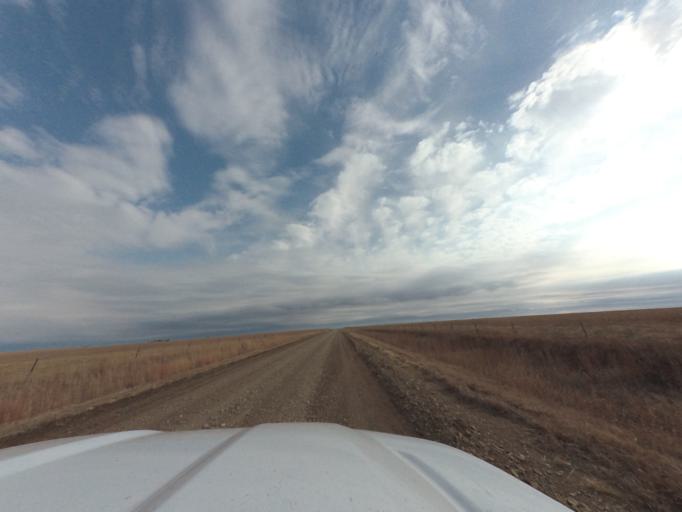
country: US
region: Kansas
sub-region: Chase County
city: Cottonwood Falls
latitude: 38.2170
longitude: -96.7249
